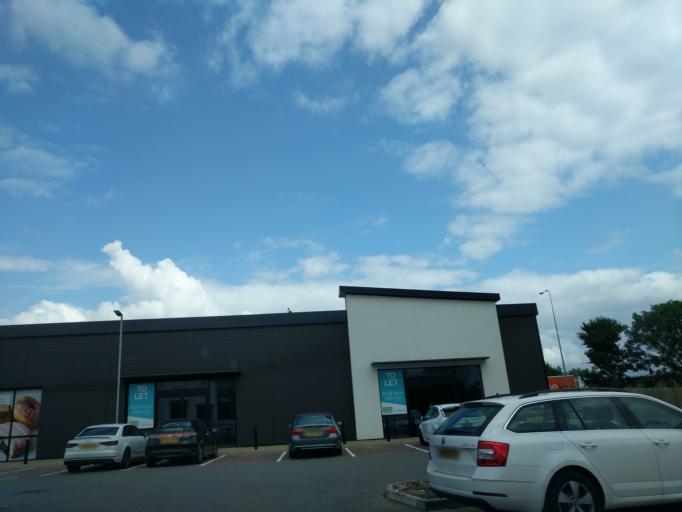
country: GB
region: England
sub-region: Cambridgeshire
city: Brampton
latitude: 52.3323
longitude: -0.2507
